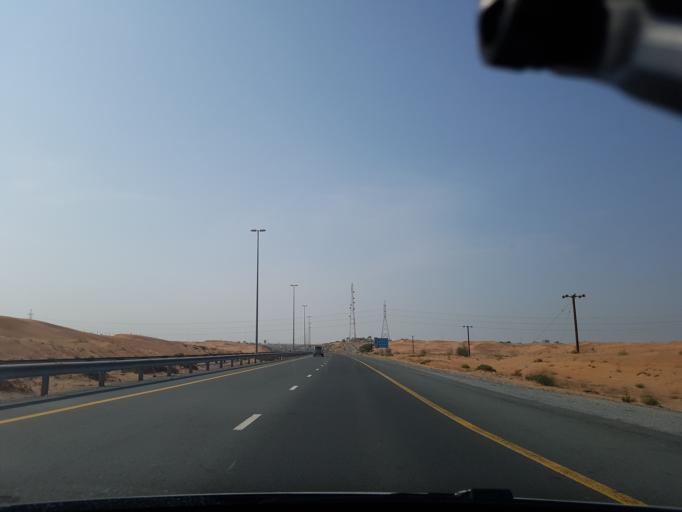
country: AE
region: Umm al Qaywayn
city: Umm al Qaywayn
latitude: 25.5249
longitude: 55.7328
